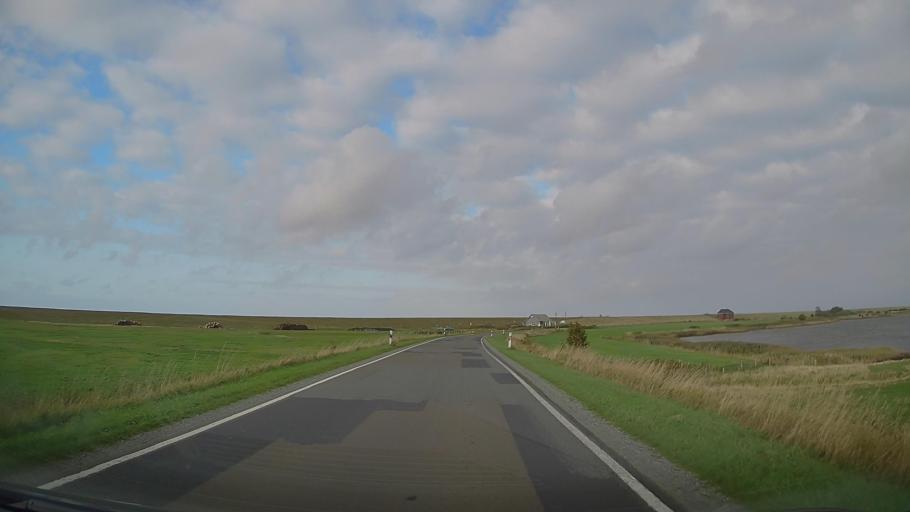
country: DE
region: Schleswig-Holstein
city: Tetenbull
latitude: 54.4058
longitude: 8.8211
